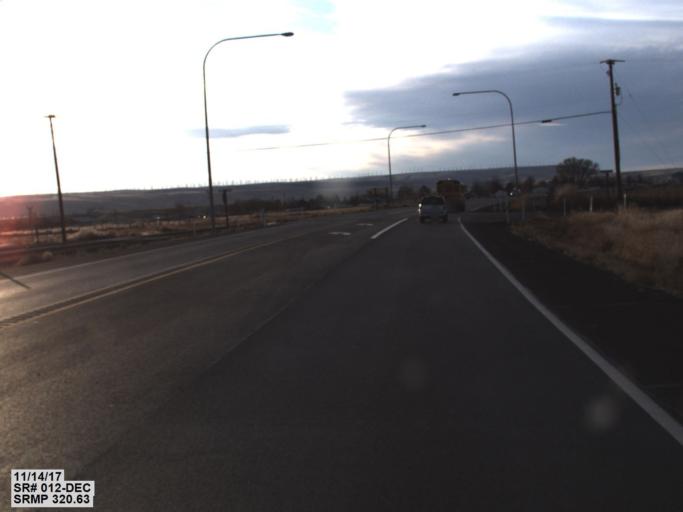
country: US
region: Washington
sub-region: Walla Walla County
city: Garrett
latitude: 46.0395
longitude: -118.6582
